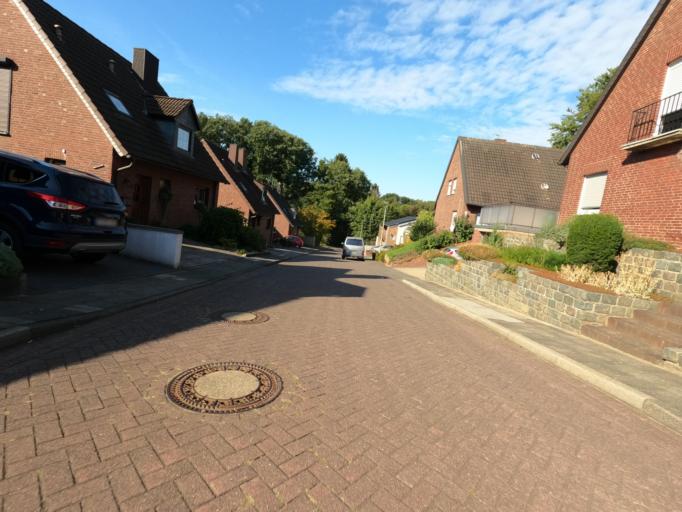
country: DE
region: North Rhine-Westphalia
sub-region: Regierungsbezirk Koln
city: Wassenberg
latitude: 51.0939
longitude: 6.1917
